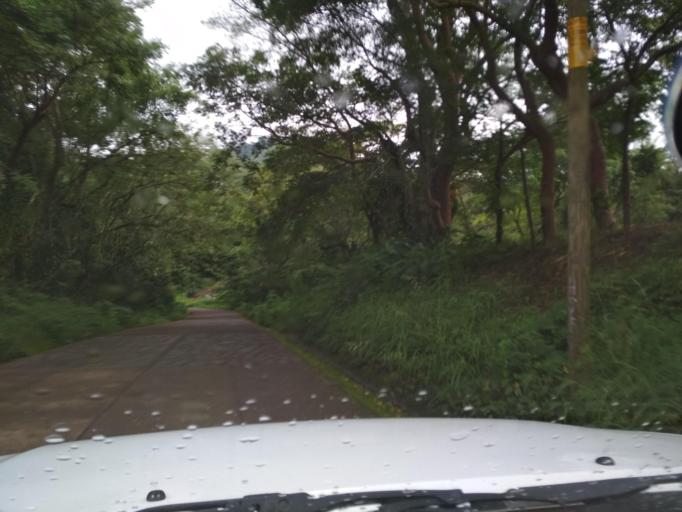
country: MX
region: Veracruz
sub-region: San Andres Tuxtla
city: San Isidro Xoteapan (San Isidro Texcaltitan)
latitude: 18.4553
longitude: -95.2323
